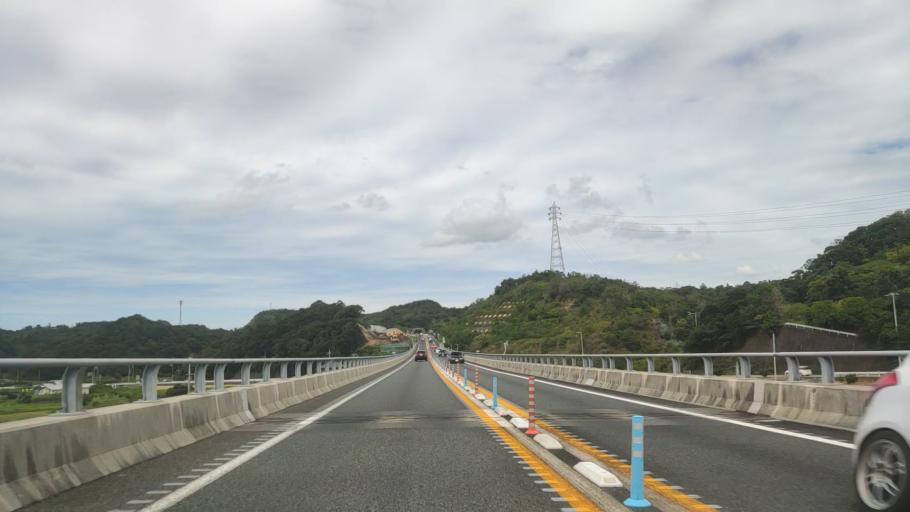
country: JP
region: Wakayama
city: Gobo
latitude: 33.8687
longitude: 135.1896
